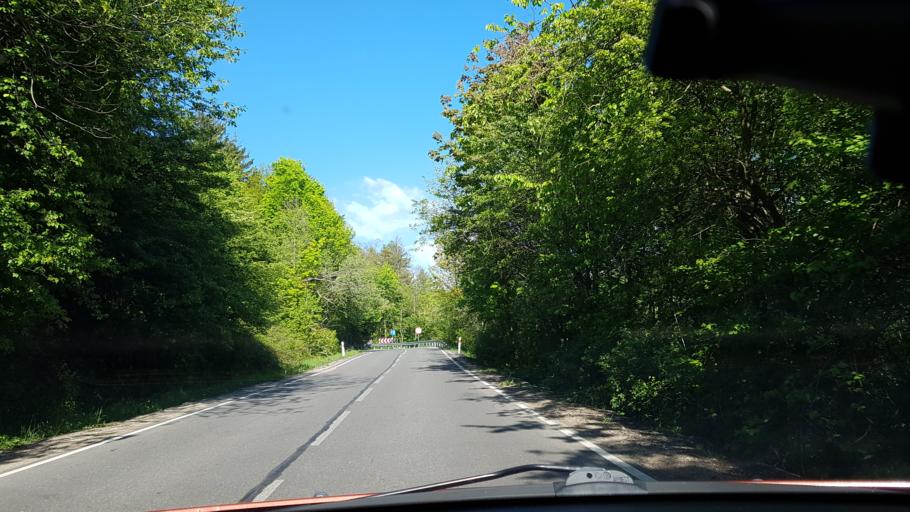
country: PL
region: Lower Silesian Voivodeship
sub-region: Powiat klodzki
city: Bozkow
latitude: 50.5709
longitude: 16.6241
